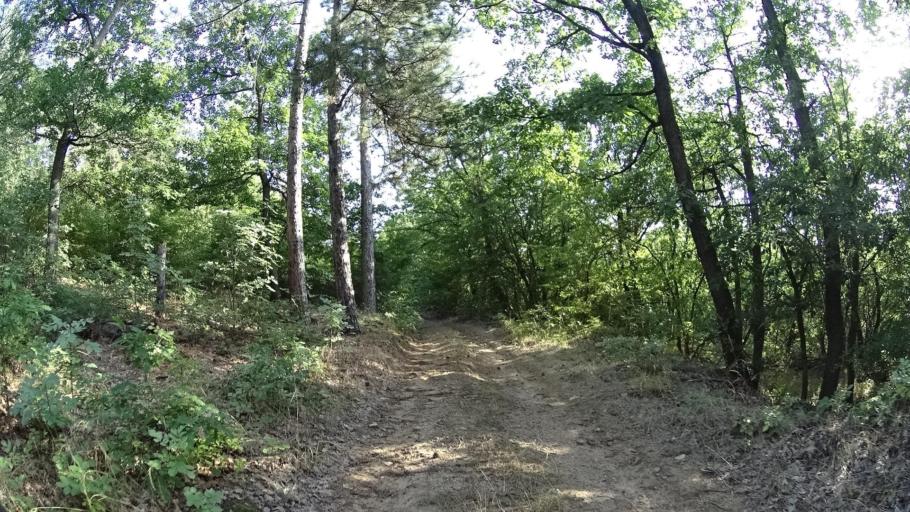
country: BG
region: Plovdiv
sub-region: Obshtina Plovdiv
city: Plovdiv
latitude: 42.0586
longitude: 24.6868
